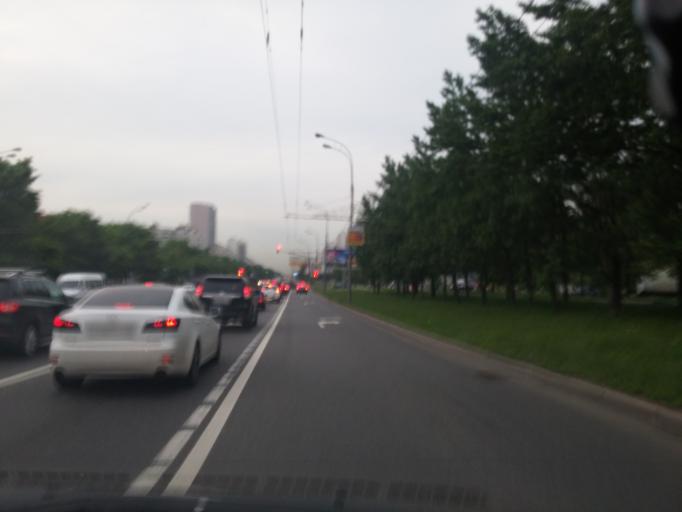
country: RU
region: Moscow
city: Altuf'yevskiy
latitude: 55.8858
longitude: 37.5869
